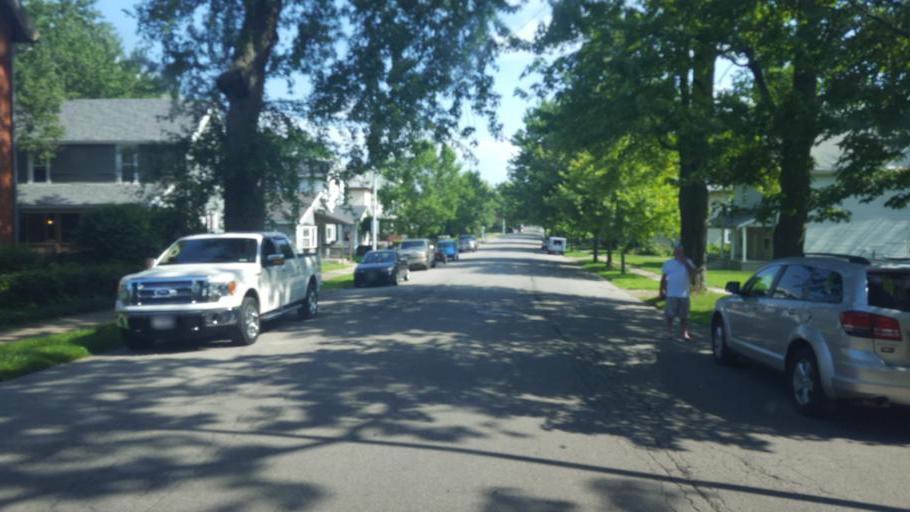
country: US
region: Ohio
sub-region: Crawford County
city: Galion
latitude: 40.7375
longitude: -82.7894
